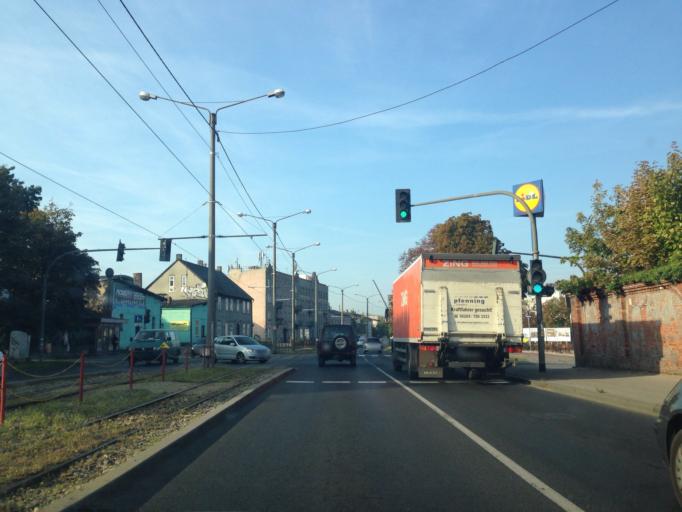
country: PL
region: Kujawsko-Pomorskie
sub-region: Torun
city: Torun
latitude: 53.0173
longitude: 18.6371
